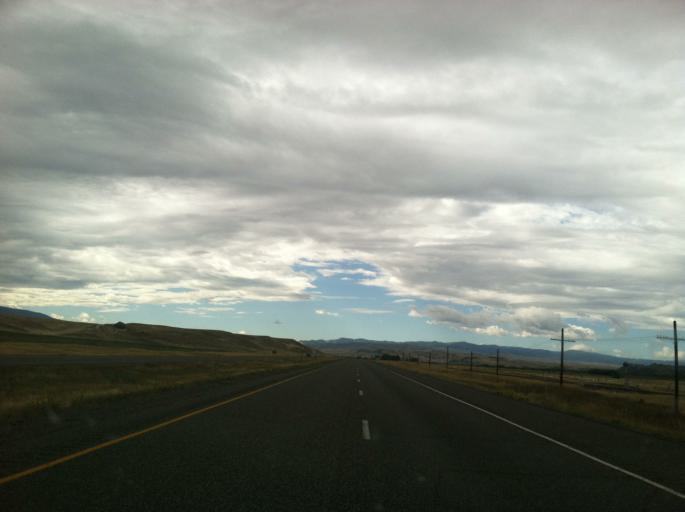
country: US
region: Montana
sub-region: Park County
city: Livingston
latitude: 45.7135
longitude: -110.4117
